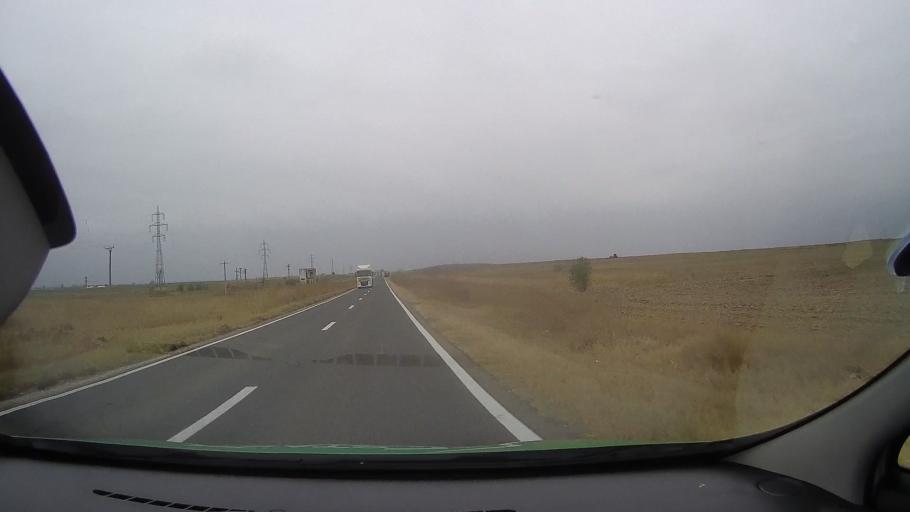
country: RO
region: Constanta
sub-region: Comuna Ciobanu
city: Ciobanu
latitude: 44.6959
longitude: 27.9880
